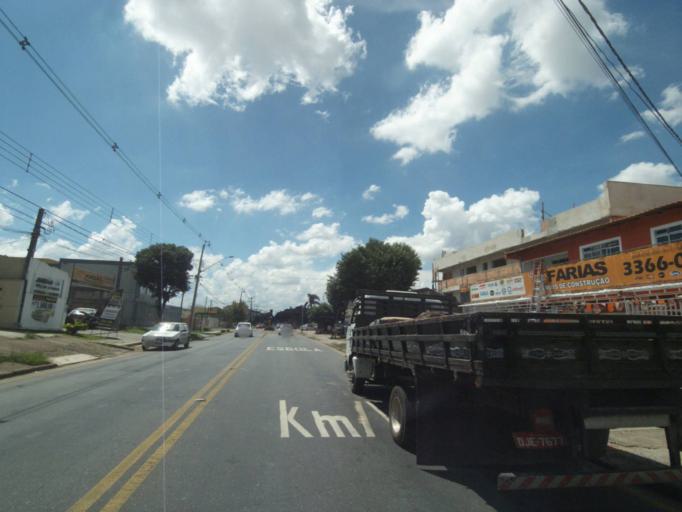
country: BR
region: Parana
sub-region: Pinhais
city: Pinhais
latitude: -25.4477
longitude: -49.2052
